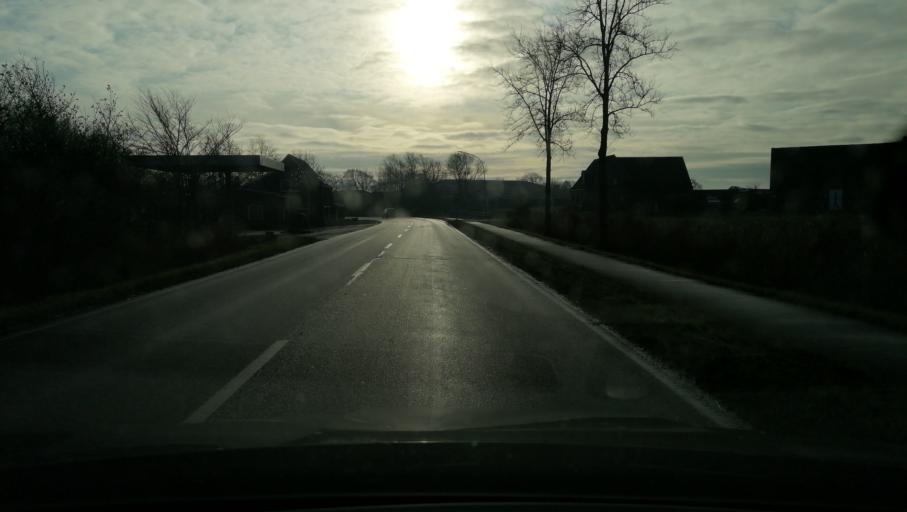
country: DE
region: Schleswig-Holstein
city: Epenwohrden
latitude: 54.1164
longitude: 9.0141
